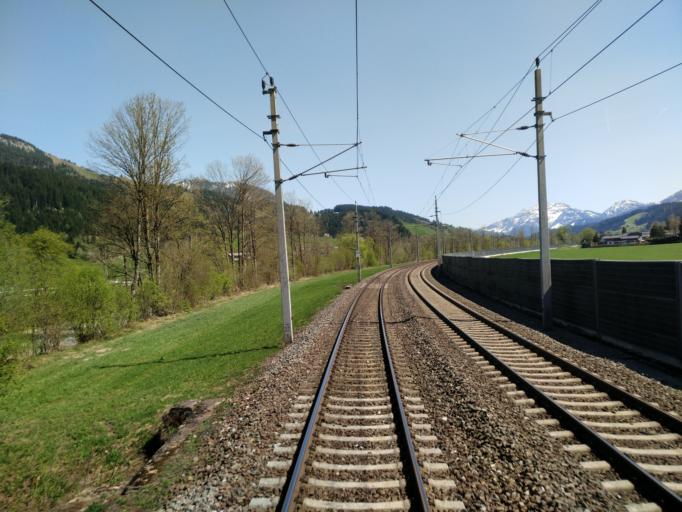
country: AT
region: Tyrol
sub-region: Politischer Bezirk Kitzbuhel
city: Sankt Johann in Tirol
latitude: 47.5177
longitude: 12.4491
